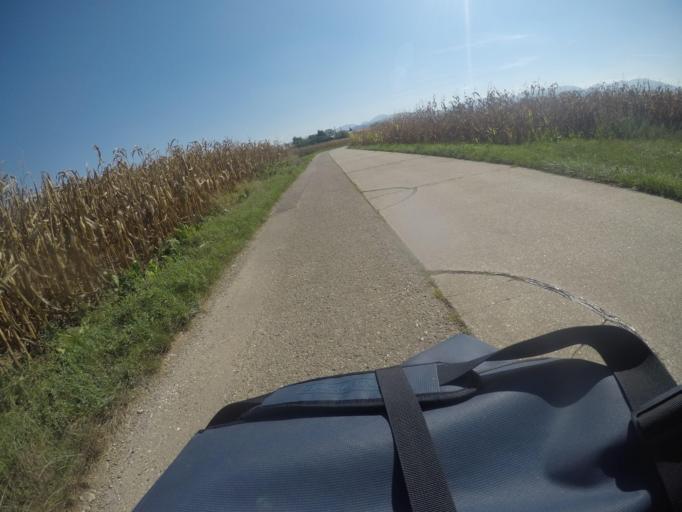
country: DE
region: Baden-Wuerttemberg
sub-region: Freiburg Region
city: Heitersheim
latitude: 47.8766
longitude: 7.6399
